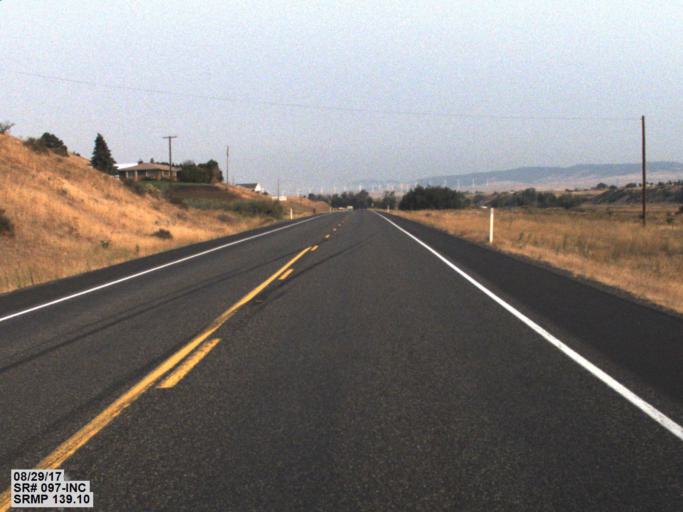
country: US
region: Washington
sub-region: Kittitas County
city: Ellensburg
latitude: 47.0689
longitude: -120.6255
